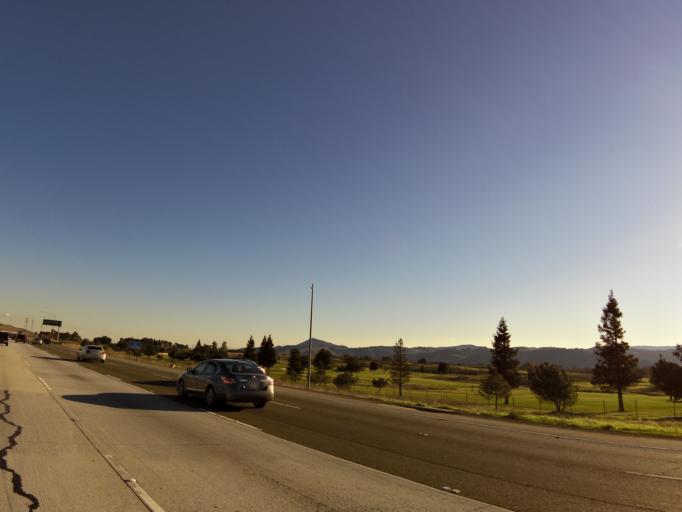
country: US
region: California
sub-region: Santa Clara County
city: Morgan Hill
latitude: 37.1949
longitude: -121.6994
